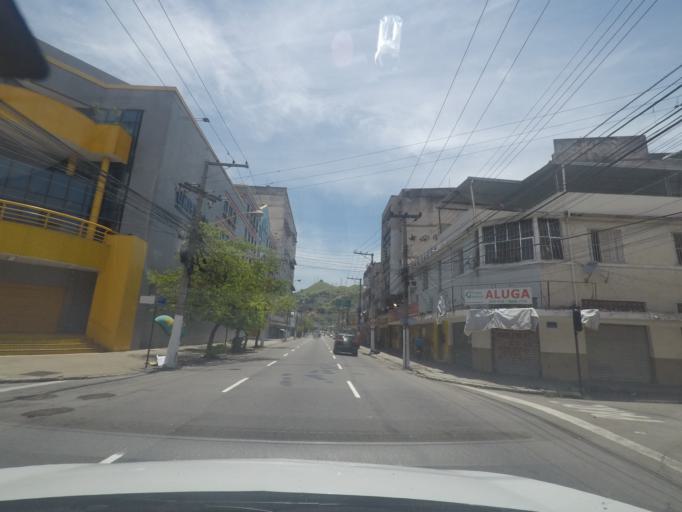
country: BR
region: Rio de Janeiro
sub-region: Niteroi
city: Niteroi
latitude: -22.8894
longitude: -43.1177
